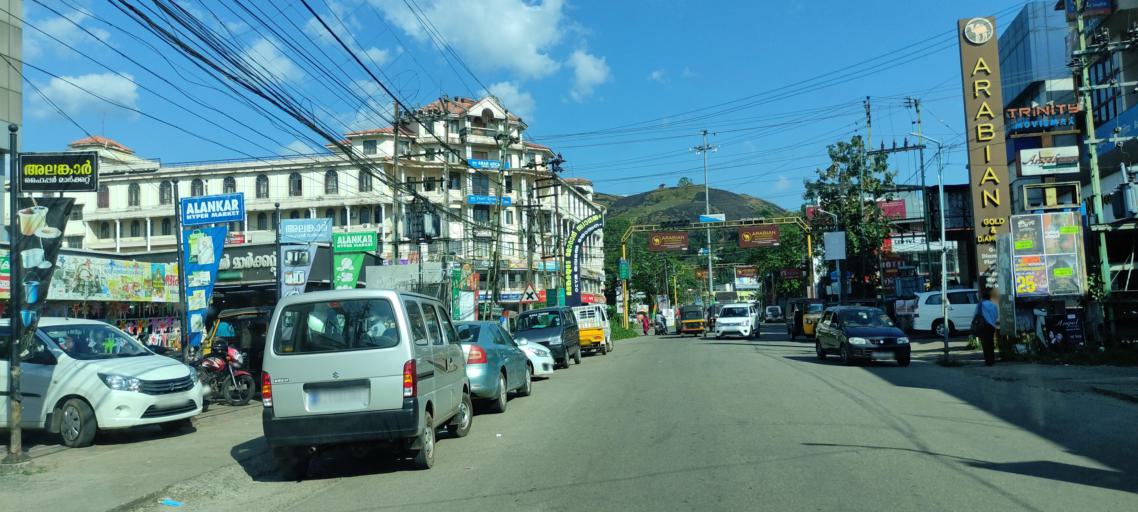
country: IN
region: Kerala
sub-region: Pattanamtitta
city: Pathanamthitta
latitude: 9.2650
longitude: 76.7895
